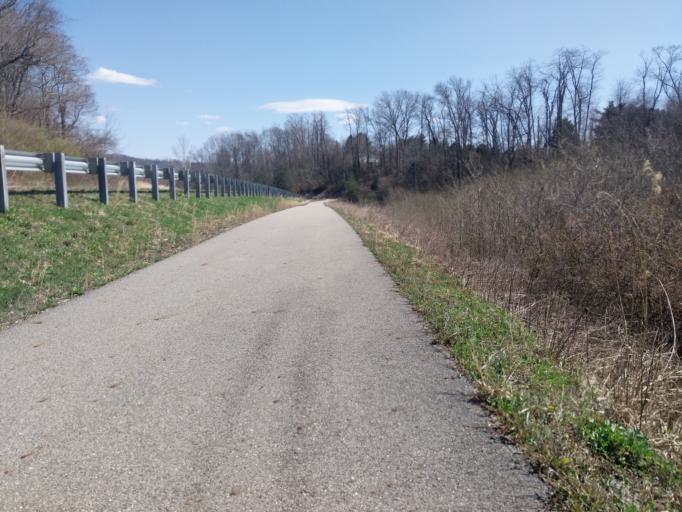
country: US
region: Ohio
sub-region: Athens County
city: The Plains
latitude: 39.3658
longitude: -82.1218
